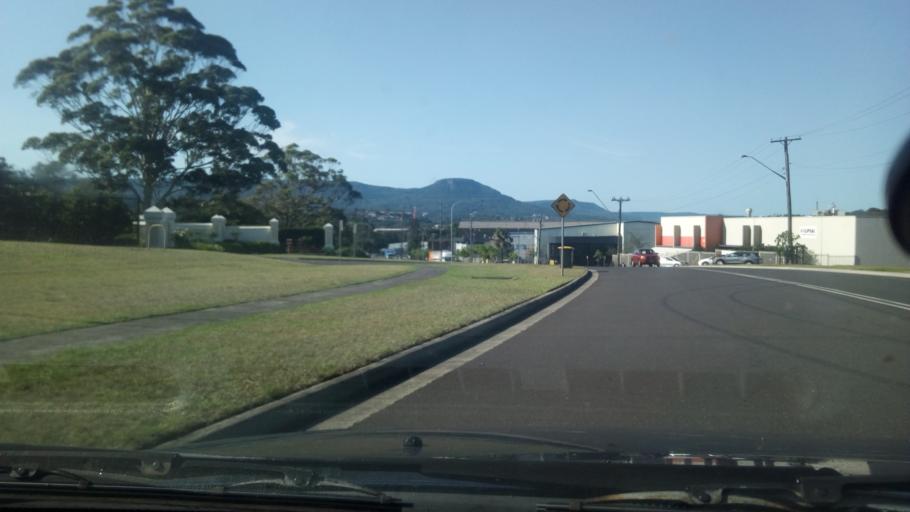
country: AU
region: New South Wales
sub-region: Wollongong
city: Berkeley
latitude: -34.4651
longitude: 150.8542
